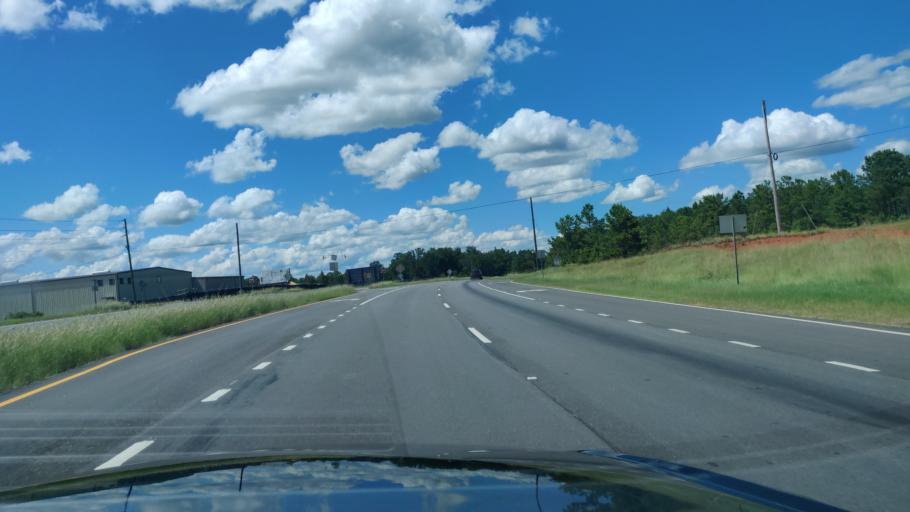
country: US
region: Georgia
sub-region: Stewart County
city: Richland
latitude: 32.0883
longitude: -84.6771
